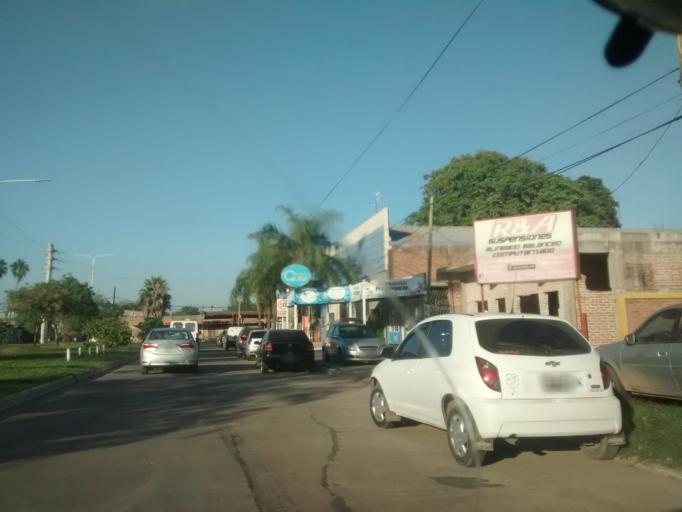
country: AR
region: Chaco
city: Resistencia
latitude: -27.4695
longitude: -58.9930
